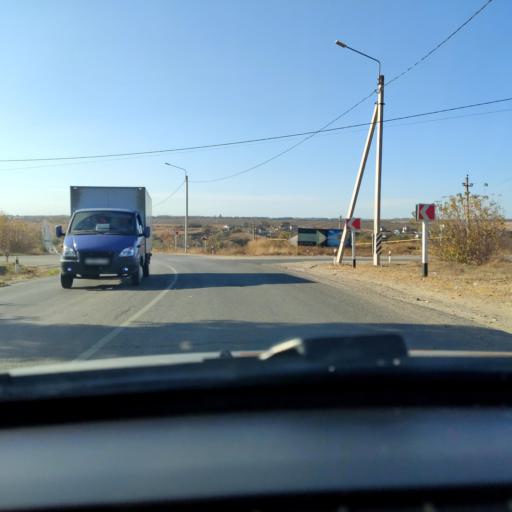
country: RU
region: Voronezj
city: Semiluki
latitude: 51.7280
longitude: 39.0257
